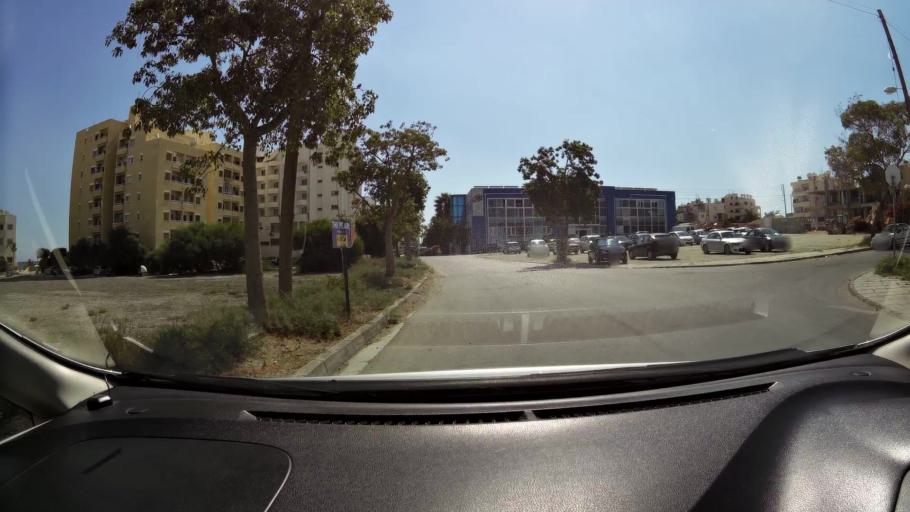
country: CY
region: Larnaka
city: Larnaca
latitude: 34.8945
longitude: 33.6375
